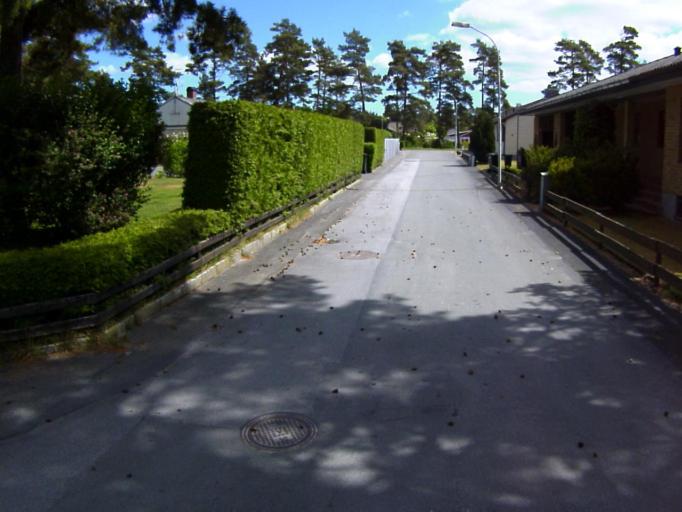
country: SE
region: Skane
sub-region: Kristianstads Kommun
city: Ahus
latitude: 55.9449
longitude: 14.2772
